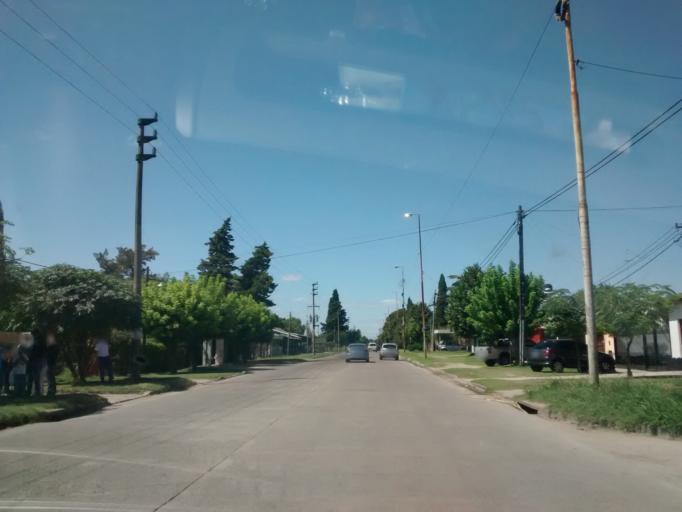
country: AR
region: Buenos Aires
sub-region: Partido de Berisso
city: Berisso
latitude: -34.8816
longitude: -57.8442
